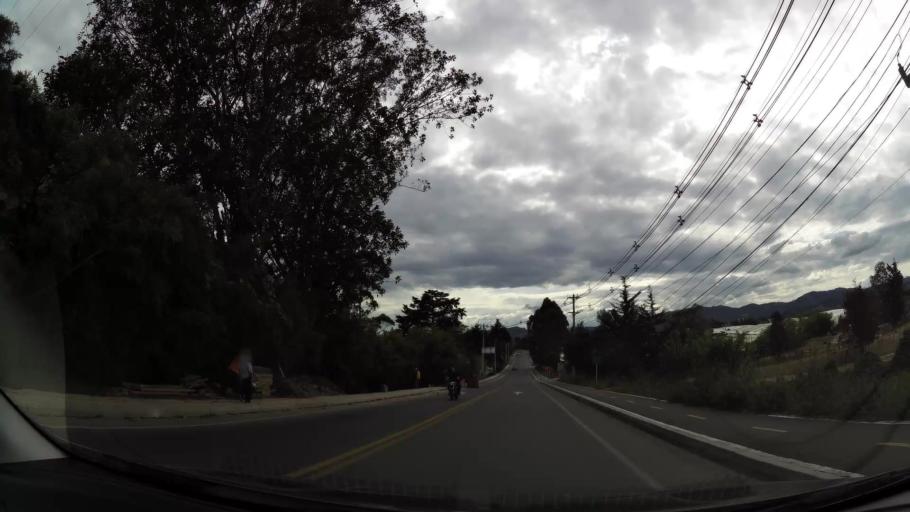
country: CO
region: Antioquia
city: Rionegro
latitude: 6.1526
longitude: -75.4128
